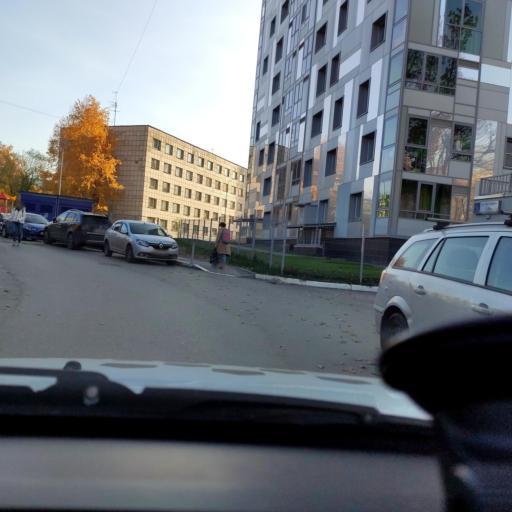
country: RU
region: Perm
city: Perm
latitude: 58.0021
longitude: 56.2455
